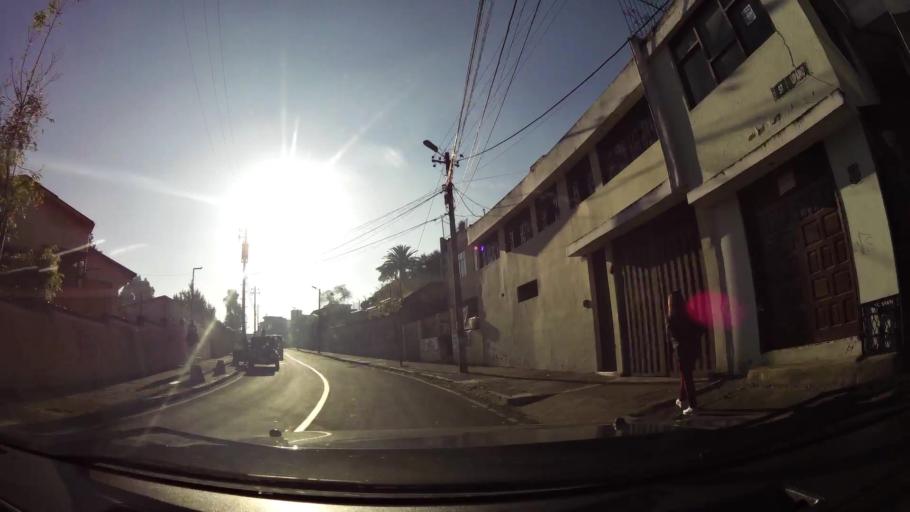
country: EC
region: Pichincha
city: Quito
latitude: -0.2362
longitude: -78.5138
